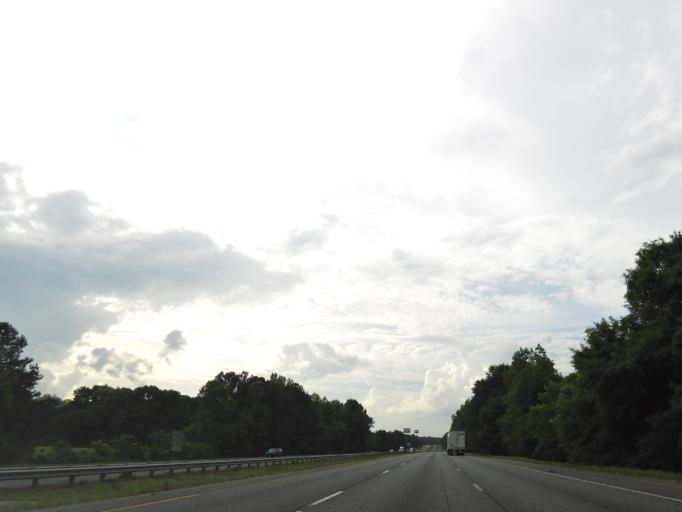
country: US
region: Georgia
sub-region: Butts County
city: Jackson
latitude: 33.2176
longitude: -84.0686
